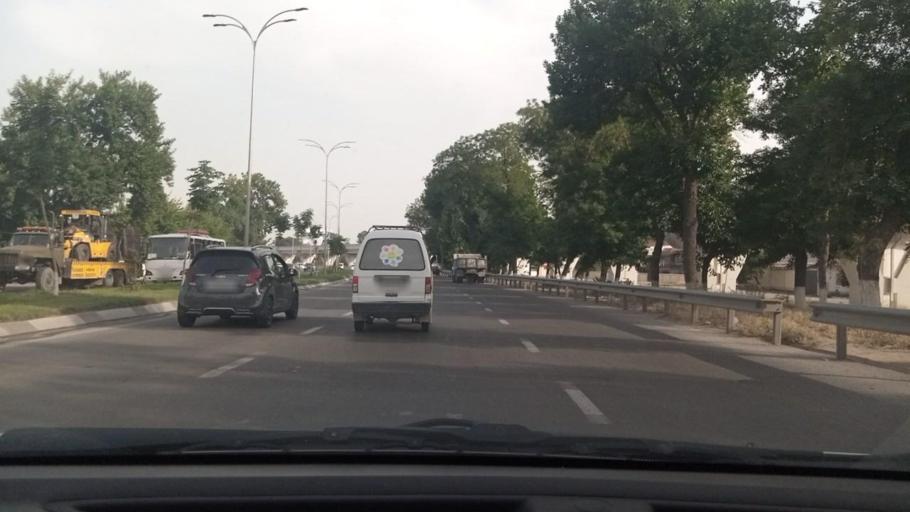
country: UZ
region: Toshkent Shahri
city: Bektemir
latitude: 41.2724
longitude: 69.3623
